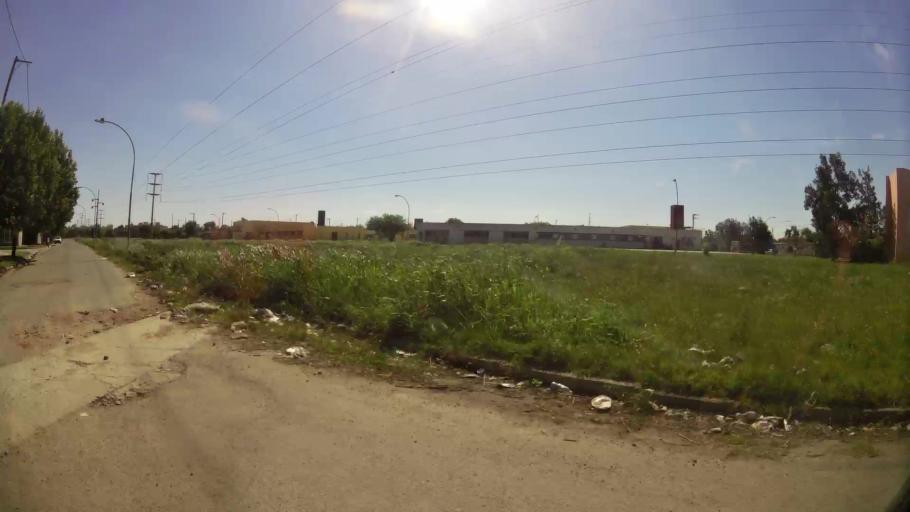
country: AR
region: Cordoba
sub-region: Departamento de Capital
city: Cordoba
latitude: -31.3643
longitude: -64.1556
